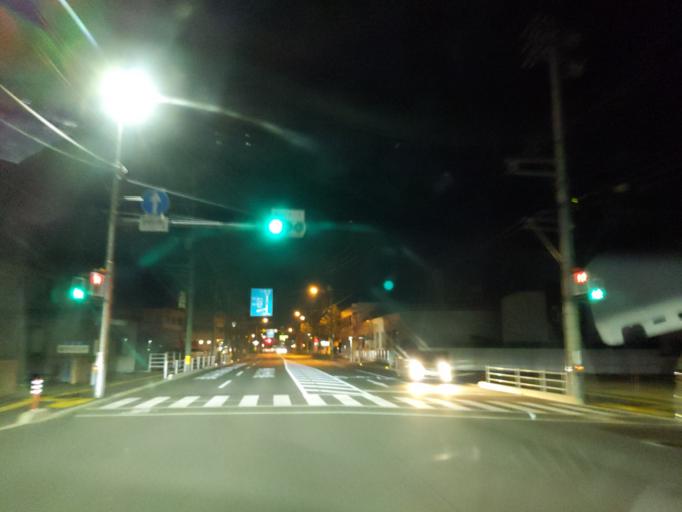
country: JP
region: Okayama
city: Okayama-shi
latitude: 34.6682
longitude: 133.9496
